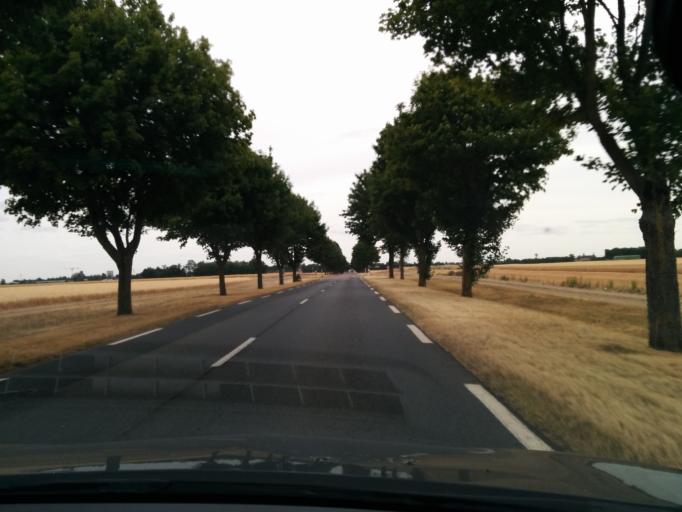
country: FR
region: Ile-de-France
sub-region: Departement de l'Essonne
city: Angerville
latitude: 48.3291
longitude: 1.9930
